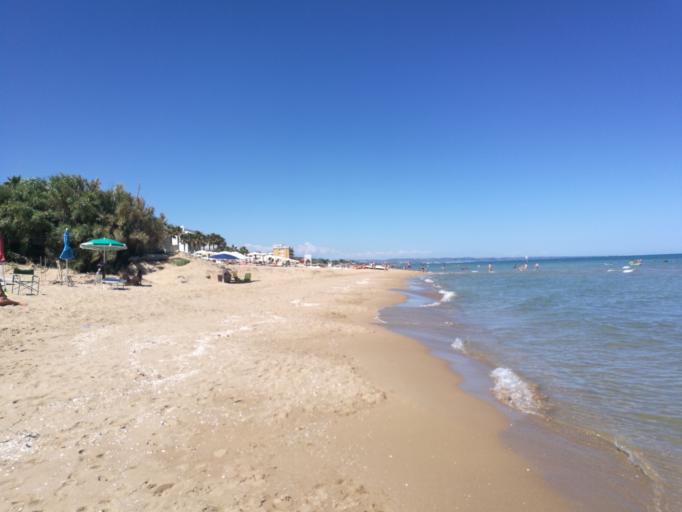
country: IT
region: Molise
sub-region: Provincia di Campobasso
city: Petacciato
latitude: 42.0197
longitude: 14.9068
